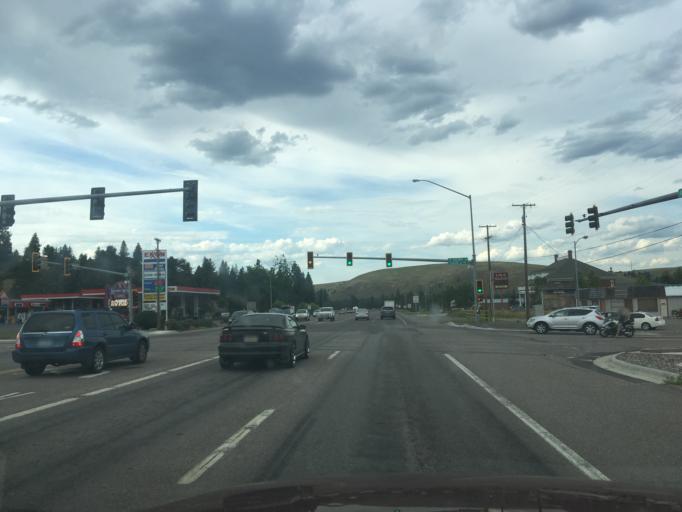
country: US
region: Montana
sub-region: Missoula County
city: Lolo
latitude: 46.7647
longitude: -114.0804
